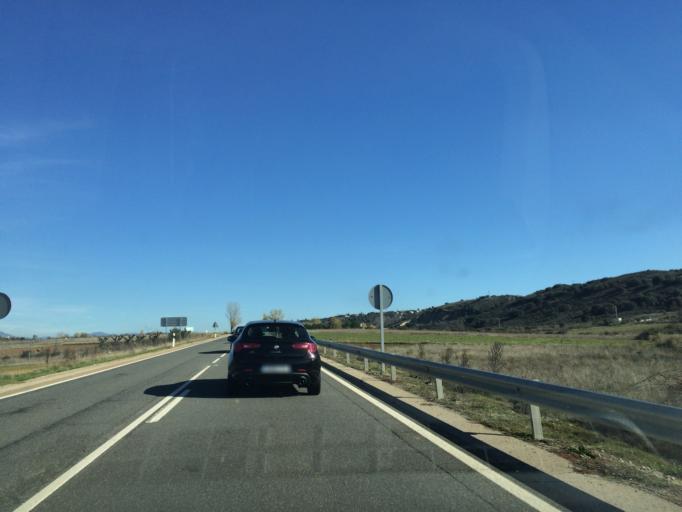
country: ES
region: Madrid
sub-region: Provincia de Madrid
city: Venturada
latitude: 40.7859
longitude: -3.6279
